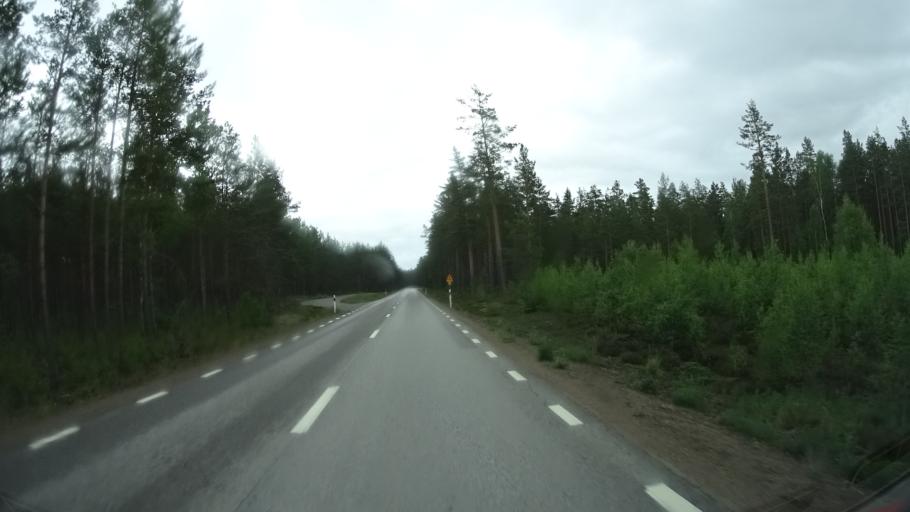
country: SE
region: Kalmar
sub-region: Hultsfreds Kommun
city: Hultsfred
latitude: 57.5224
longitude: 15.7996
